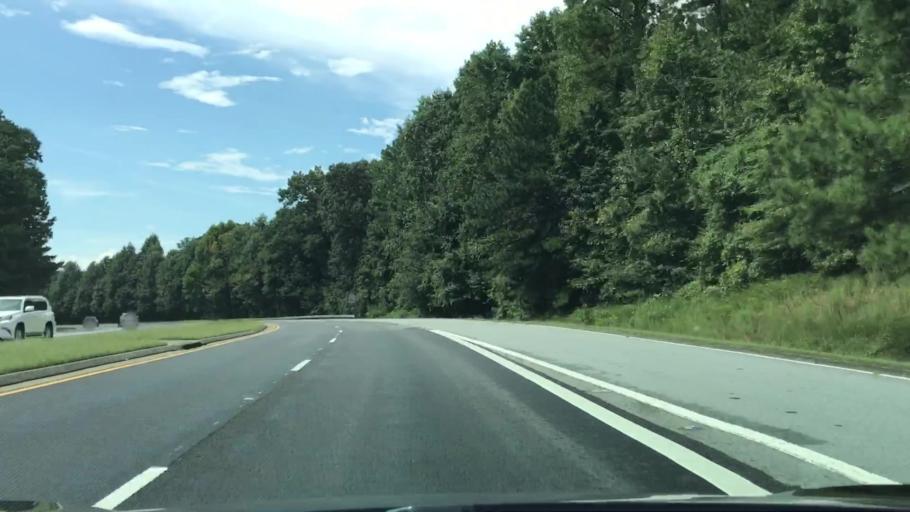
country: US
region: Georgia
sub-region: Gwinnett County
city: Lilburn
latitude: 33.9125
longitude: -84.1043
